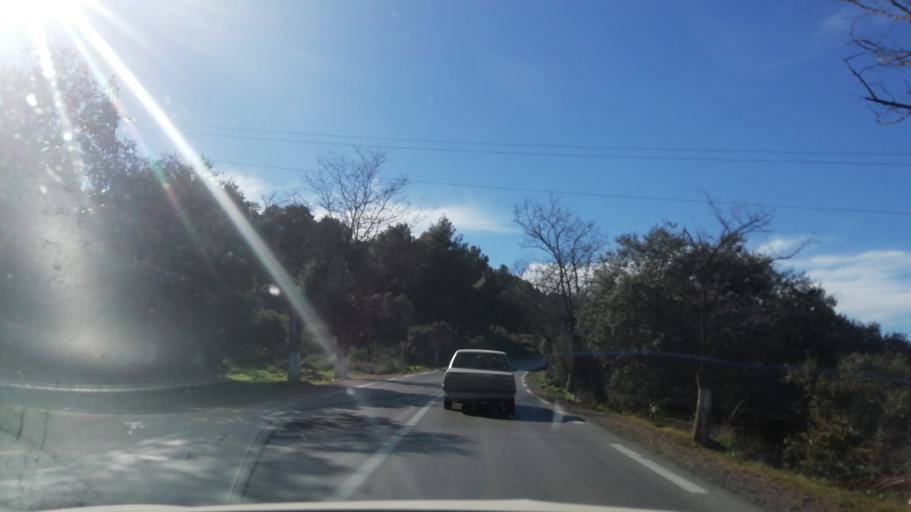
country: DZ
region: Tlemcen
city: Mansoura
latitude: 34.8507
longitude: -1.3525
